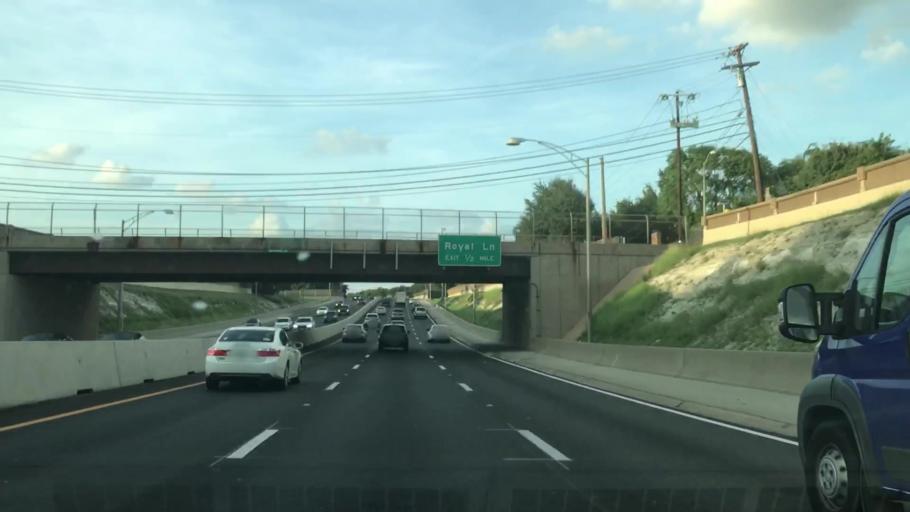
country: US
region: Texas
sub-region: Dallas County
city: University Park
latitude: 32.8862
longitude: -96.8089
